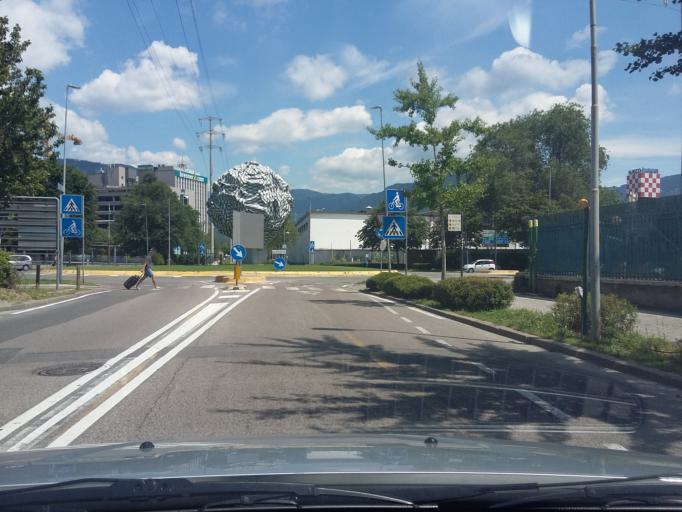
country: IT
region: Trentino-Alto Adige
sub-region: Bolzano
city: Bolzano
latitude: 46.4796
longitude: 11.3292
